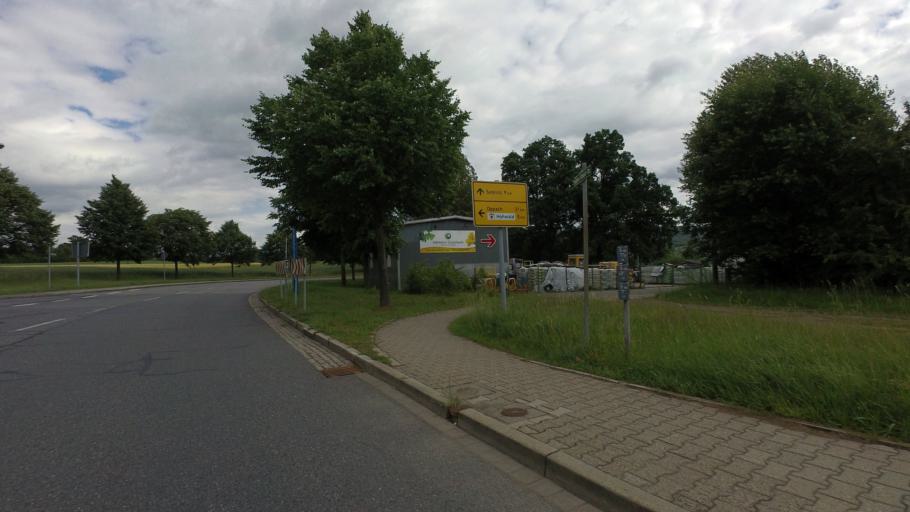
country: DE
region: Saxony
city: Neustadt in Sachsen
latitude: 51.0270
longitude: 14.2321
